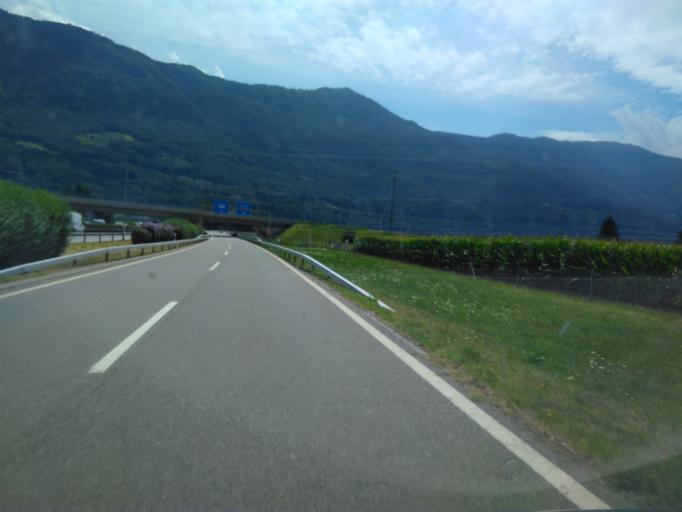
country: CH
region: Ticino
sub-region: Bellinzona District
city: Camorino
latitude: 46.1681
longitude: 8.9903
